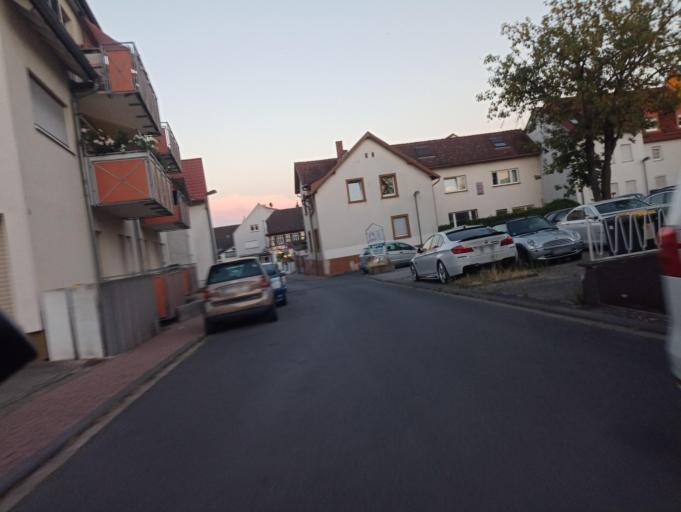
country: DE
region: Hesse
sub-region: Regierungsbezirk Darmstadt
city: Bad Homburg vor der Hoehe
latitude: 50.1896
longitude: 8.6355
